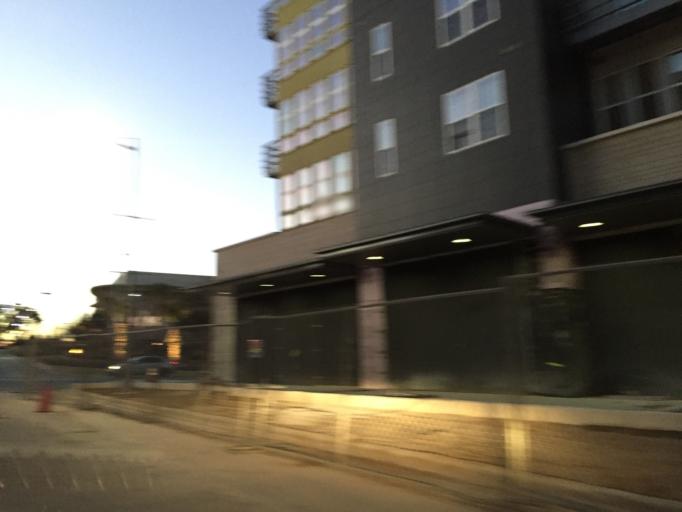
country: US
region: Texas
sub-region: Travis County
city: Wells Branch
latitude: 30.4033
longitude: -97.7234
